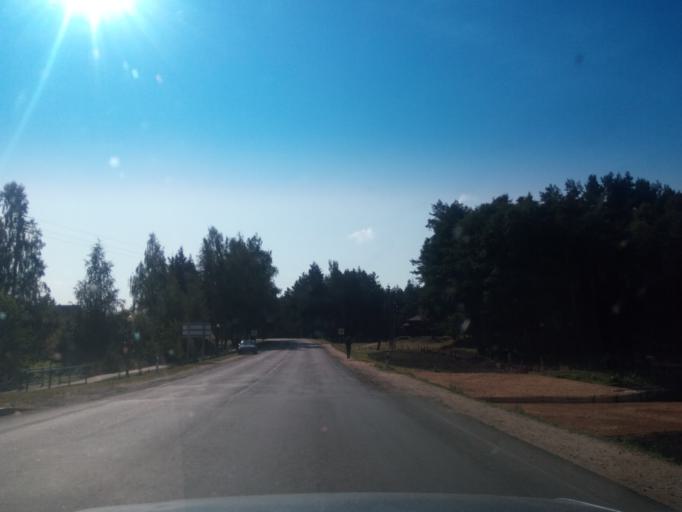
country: BY
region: Vitebsk
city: Vyerkhnyadzvinsk
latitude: 55.7609
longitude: 27.9444
